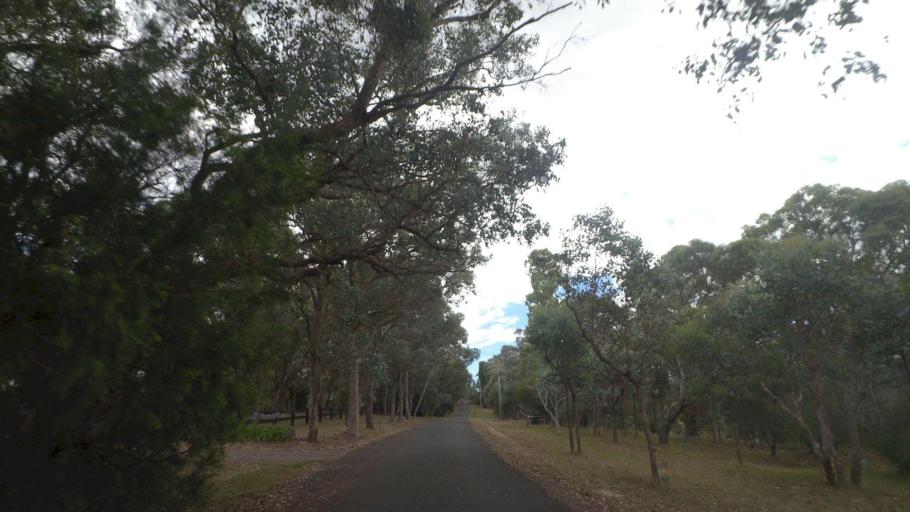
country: AU
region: Victoria
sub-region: Manningham
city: Warrandyte
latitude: -37.7498
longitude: 145.2520
